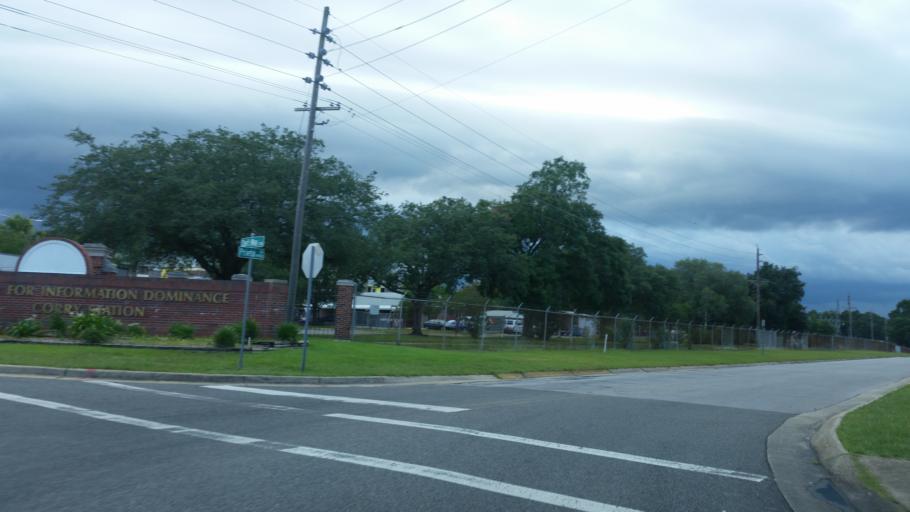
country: US
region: Florida
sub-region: Escambia County
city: West Pensacola
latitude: 30.4069
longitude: -87.2806
